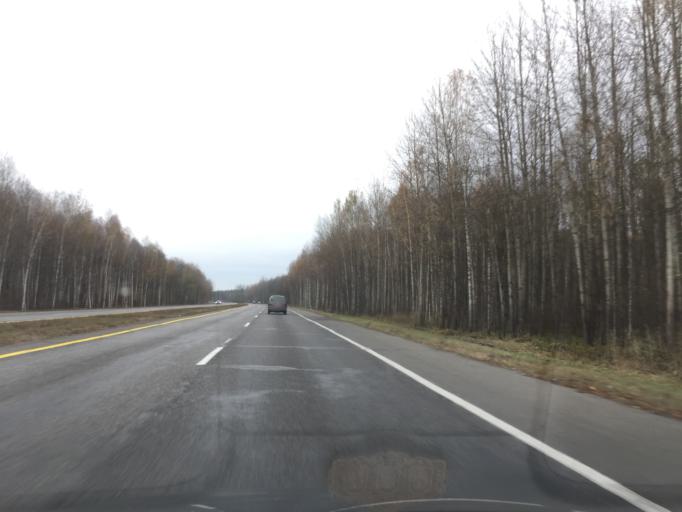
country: BY
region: Gomel
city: Kastsyukowka
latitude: 52.3568
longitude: 30.6898
